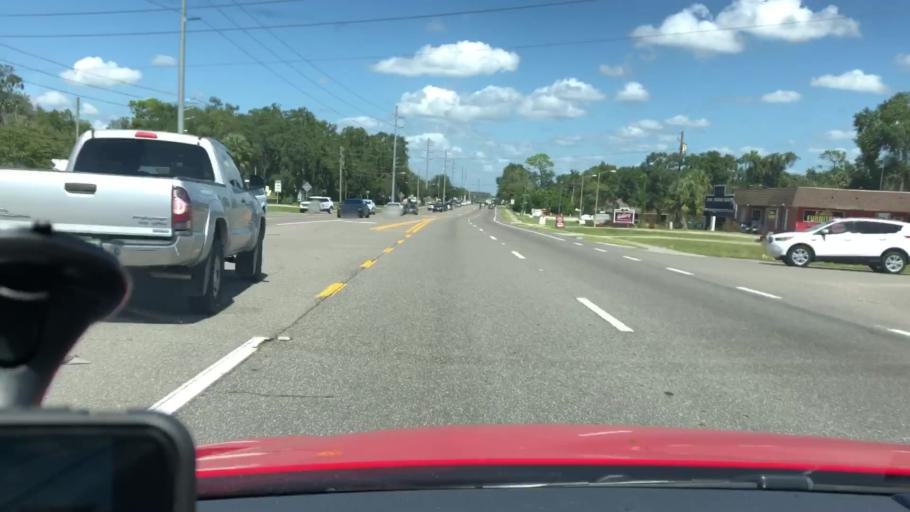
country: US
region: Florida
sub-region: Volusia County
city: Orange City
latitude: 28.9286
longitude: -81.2988
